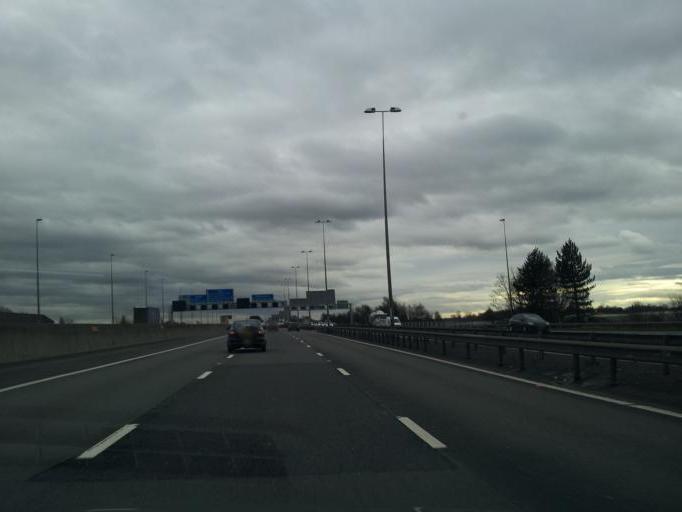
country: GB
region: England
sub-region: Warwickshire
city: Curdworth
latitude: 52.5256
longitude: -1.7286
